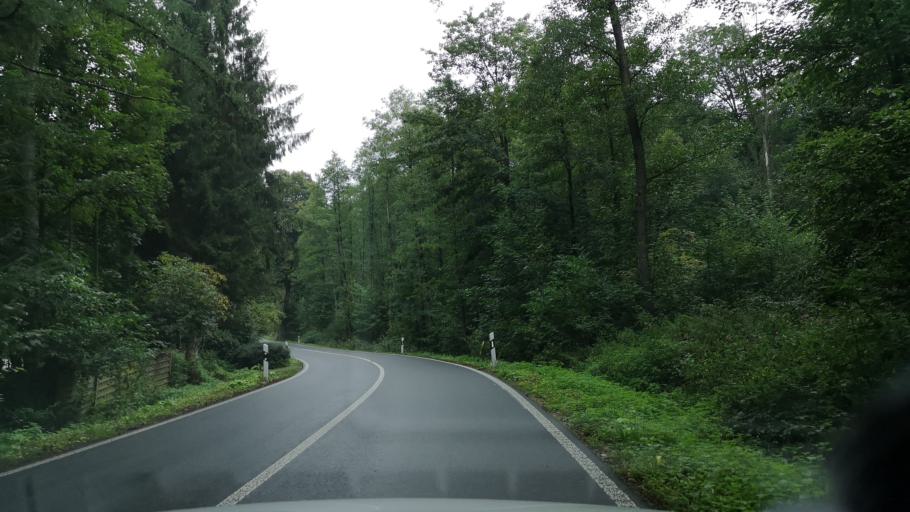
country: DE
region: North Rhine-Westphalia
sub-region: Regierungsbezirk Dusseldorf
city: Velbert
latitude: 51.3630
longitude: 7.0483
